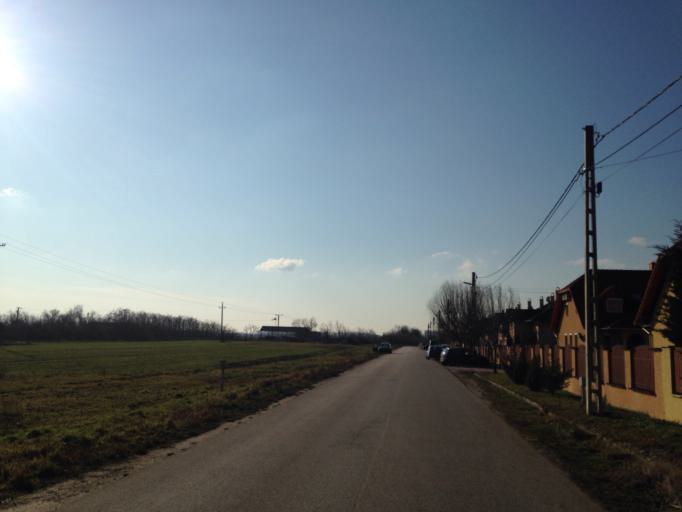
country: HU
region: Pest
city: Dunaharaszti
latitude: 47.3417
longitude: 19.0997
